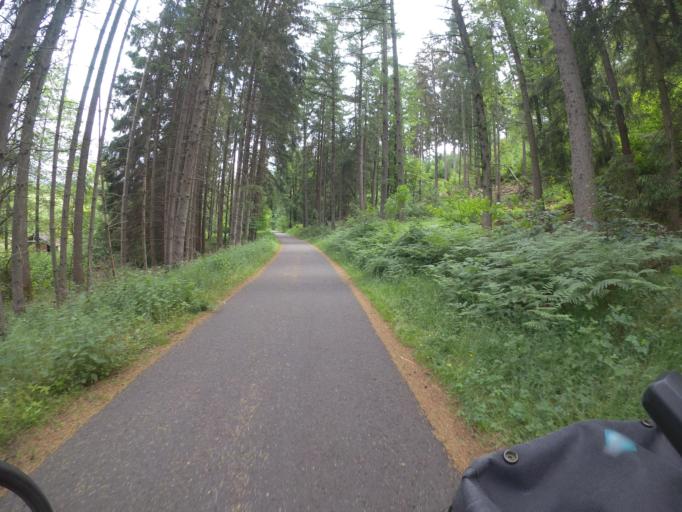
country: DE
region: Rheinland-Pfalz
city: Hinterweidenthal
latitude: 49.2003
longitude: 7.7706
